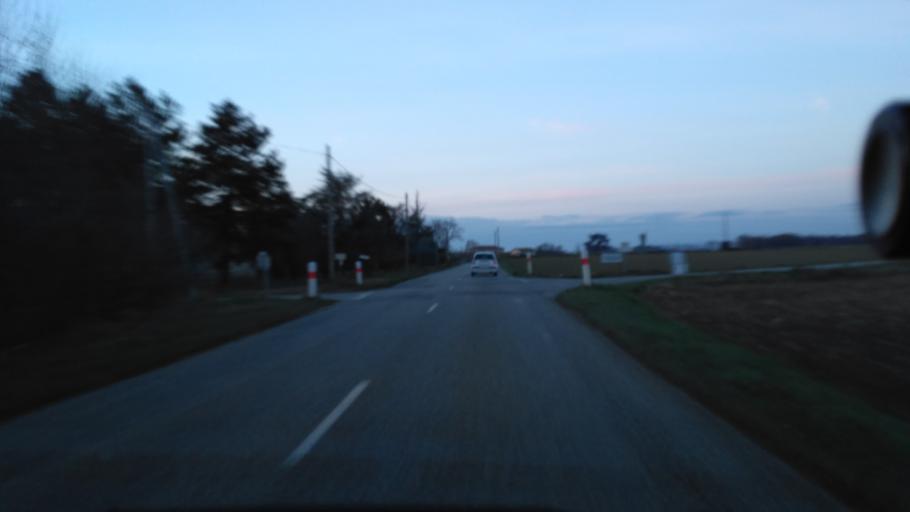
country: FR
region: Rhone-Alpes
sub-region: Departement de la Drome
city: Alixan
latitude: 44.9886
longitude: 5.0072
